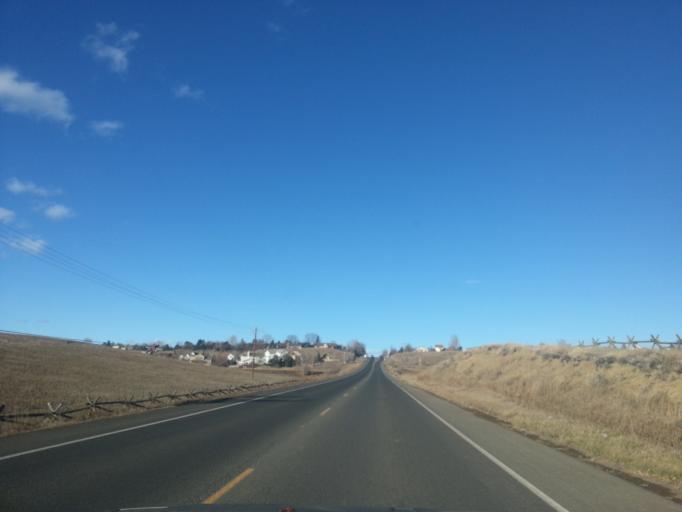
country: US
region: Colorado
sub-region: Larimer County
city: Fort Collins
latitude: 40.5202
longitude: -105.1151
